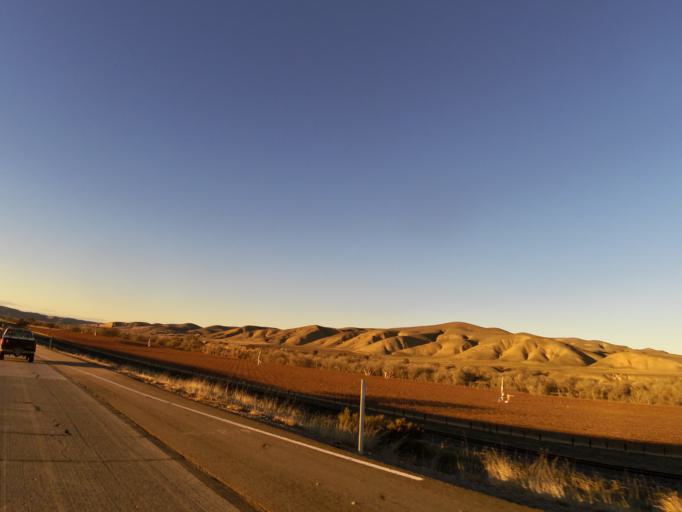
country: US
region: California
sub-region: San Luis Obispo County
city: San Miguel
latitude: 35.7710
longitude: -120.7059
